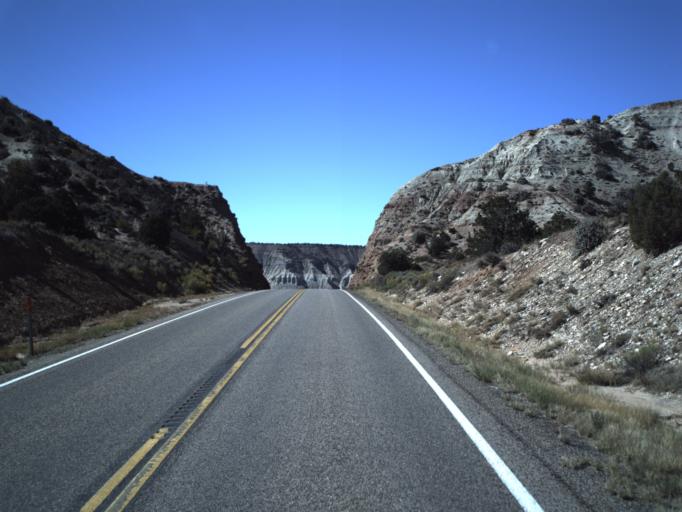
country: US
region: Utah
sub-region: Garfield County
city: Panguitch
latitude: 37.5636
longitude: -112.0362
